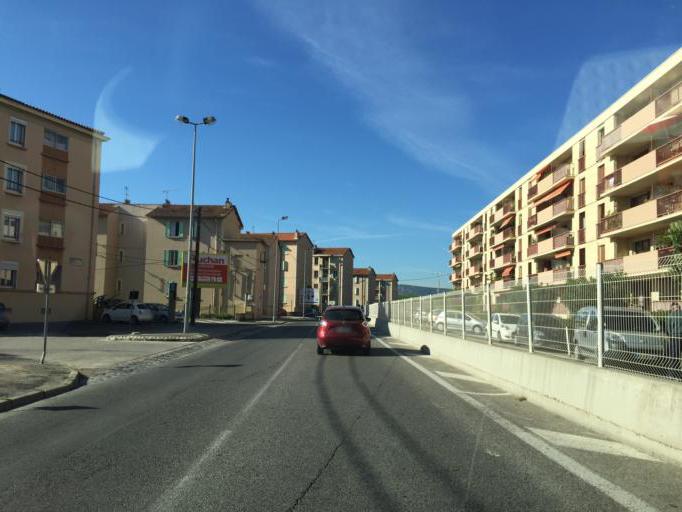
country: FR
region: Provence-Alpes-Cote d'Azur
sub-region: Departement des Bouches-du-Rhone
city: Aubagne
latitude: 43.3027
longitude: 5.5714
